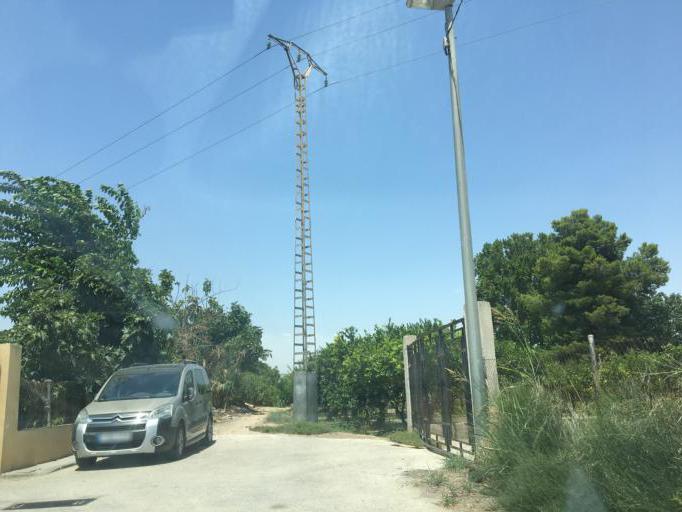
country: ES
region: Murcia
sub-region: Murcia
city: Murcia
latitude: 38.0102
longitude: -1.1122
